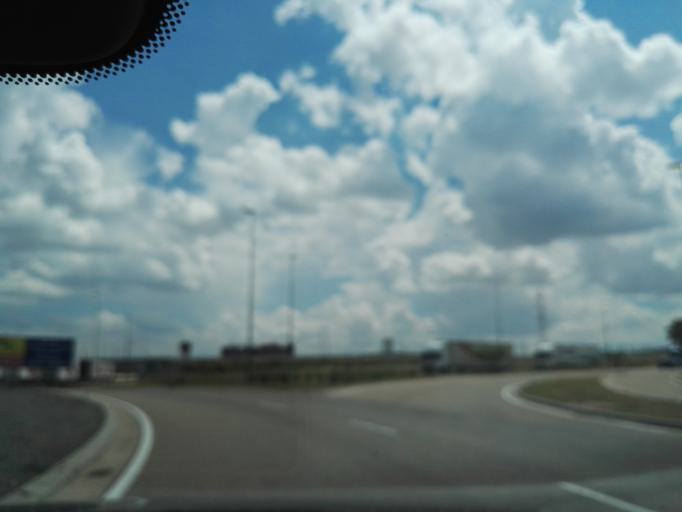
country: ES
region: Aragon
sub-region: Provincia de Zaragoza
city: Montecanal
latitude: 41.6394
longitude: -0.9930
